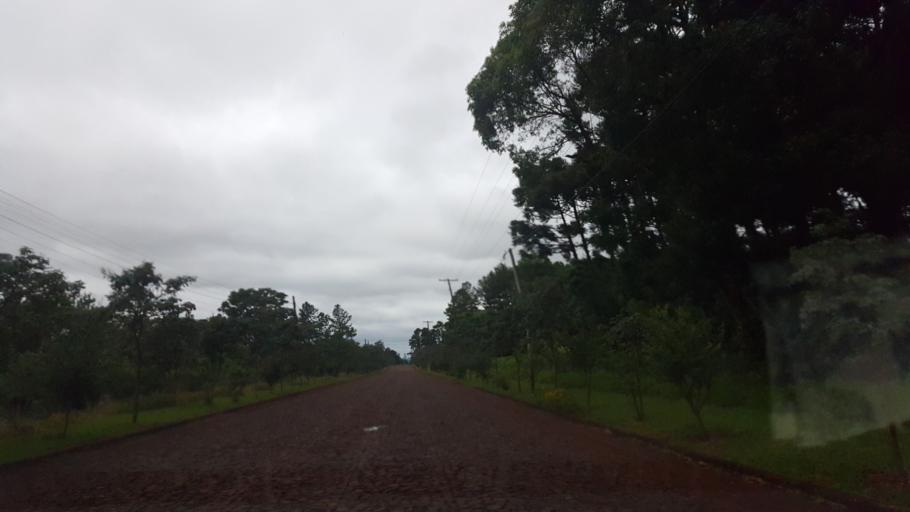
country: AR
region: Misiones
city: Capiovi
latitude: -26.9554
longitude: -55.0558
